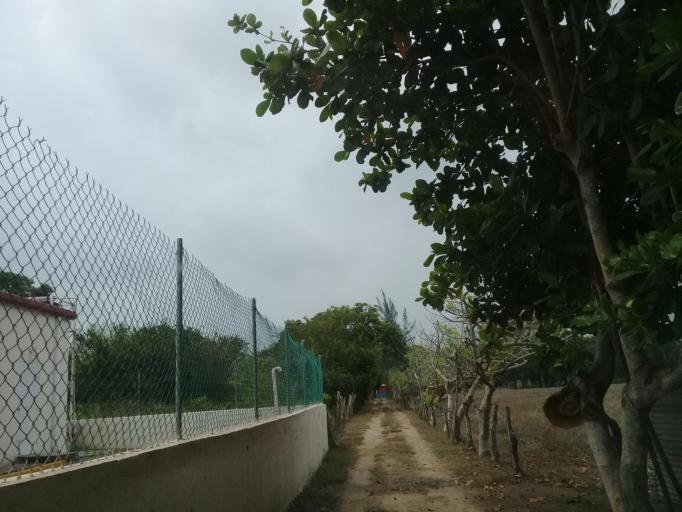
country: MX
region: Veracruz
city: Jamapa
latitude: 19.0531
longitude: -96.2029
